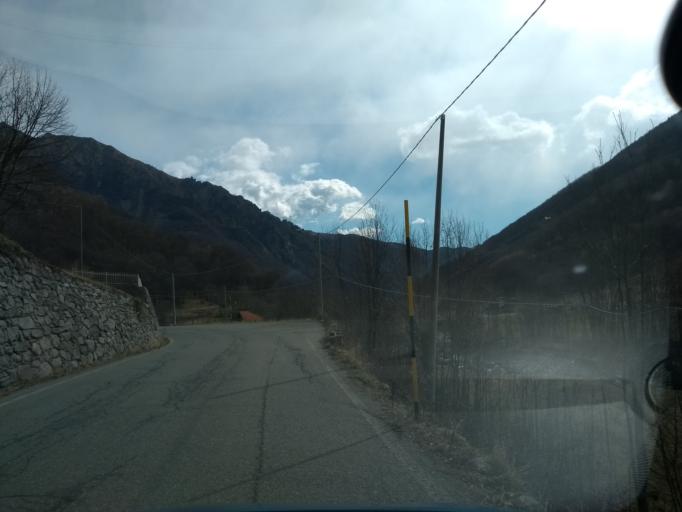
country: IT
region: Piedmont
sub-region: Provincia di Torino
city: Chialamberto
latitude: 45.3670
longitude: 7.3288
